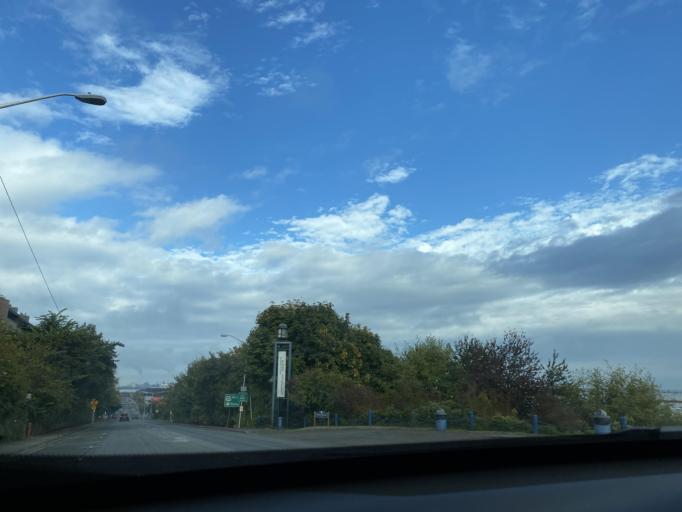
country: US
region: Washington
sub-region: Clallam County
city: Port Angeles
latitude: 48.1177
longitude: -123.4274
